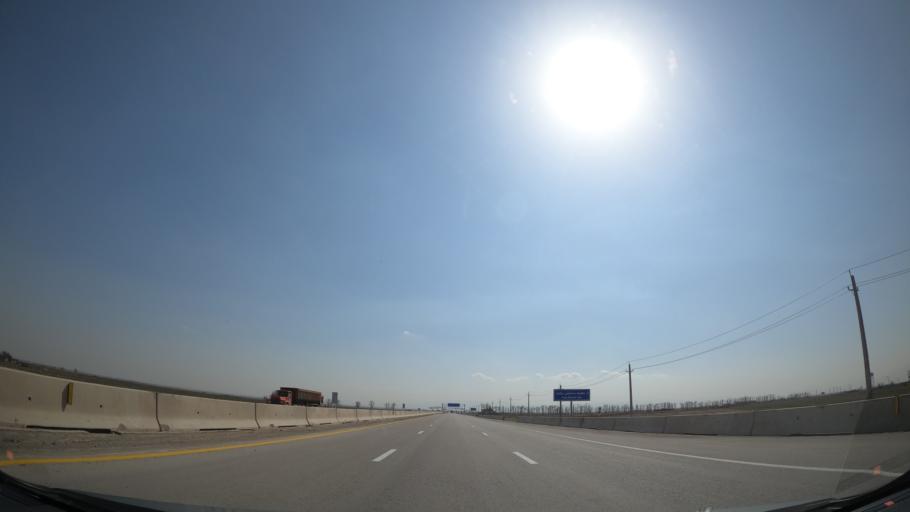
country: IR
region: Qazvin
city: Abyek
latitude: 35.9658
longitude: 50.4621
